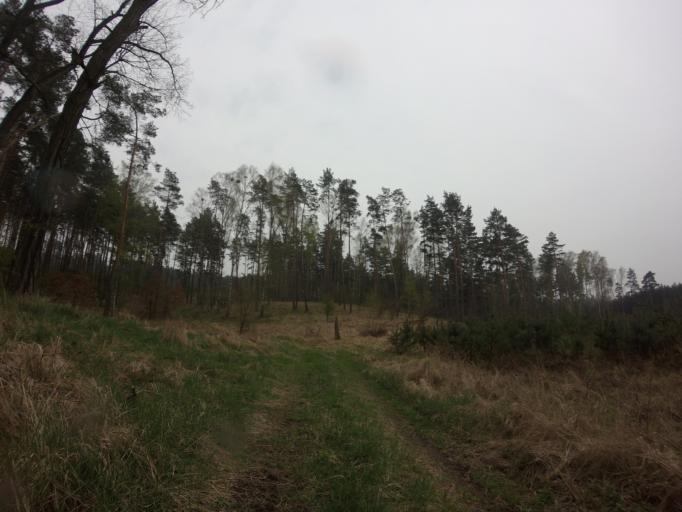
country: PL
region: West Pomeranian Voivodeship
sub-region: Powiat choszczenski
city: Recz
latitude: 53.1885
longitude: 15.5258
